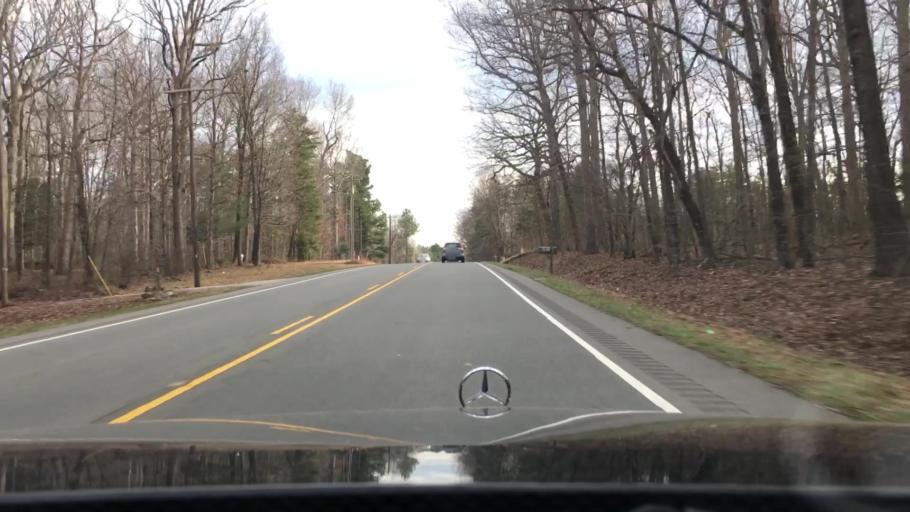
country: US
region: North Carolina
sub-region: Orange County
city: Hillsborough
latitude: 36.1961
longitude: -79.1413
